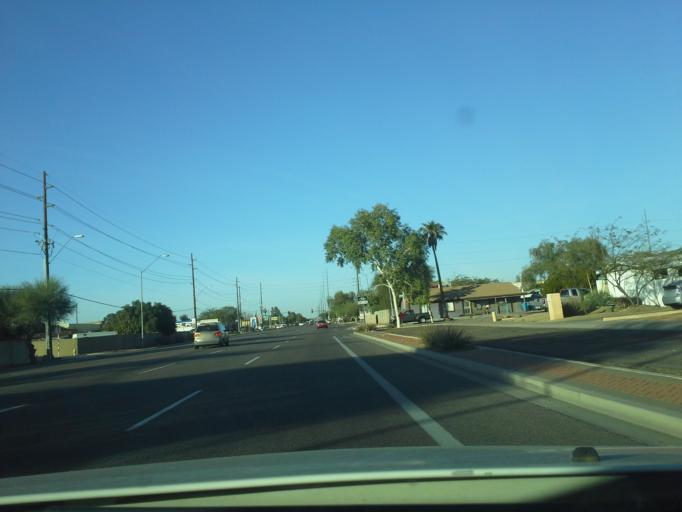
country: US
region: Arizona
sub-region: Maricopa County
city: Glendale
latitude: 33.6517
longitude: -112.1344
